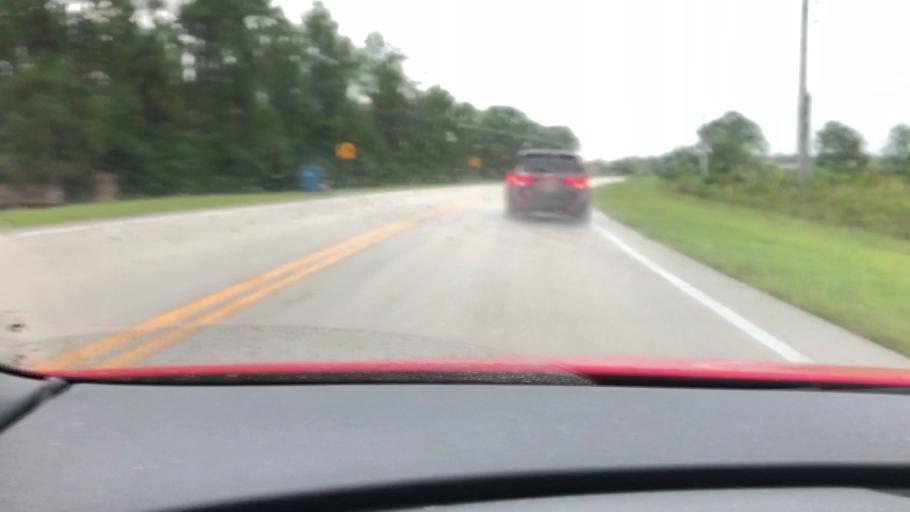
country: US
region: Florida
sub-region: Volusia County
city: Samsula-Spruce Creek
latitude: 29.0582
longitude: -81.0685
